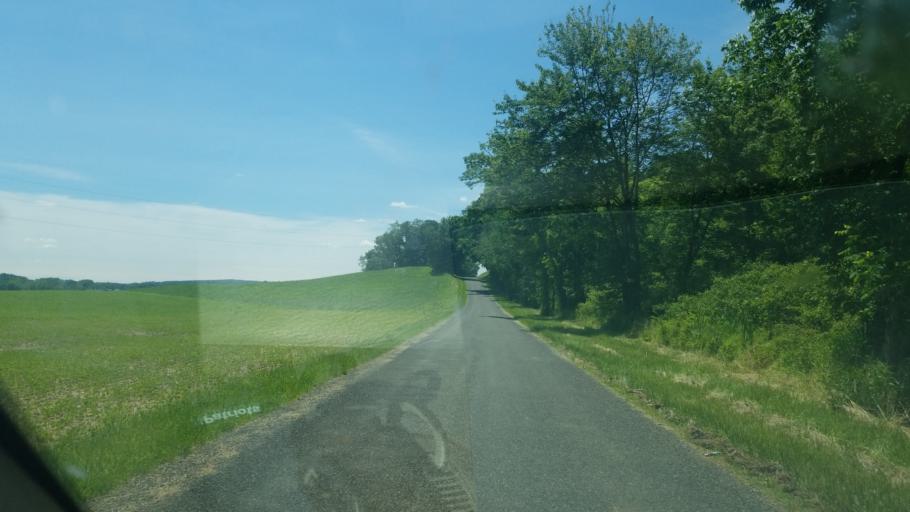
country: US
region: Ohio
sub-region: Mahoning County
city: Sebring
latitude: 40.8645
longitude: -80.9718
